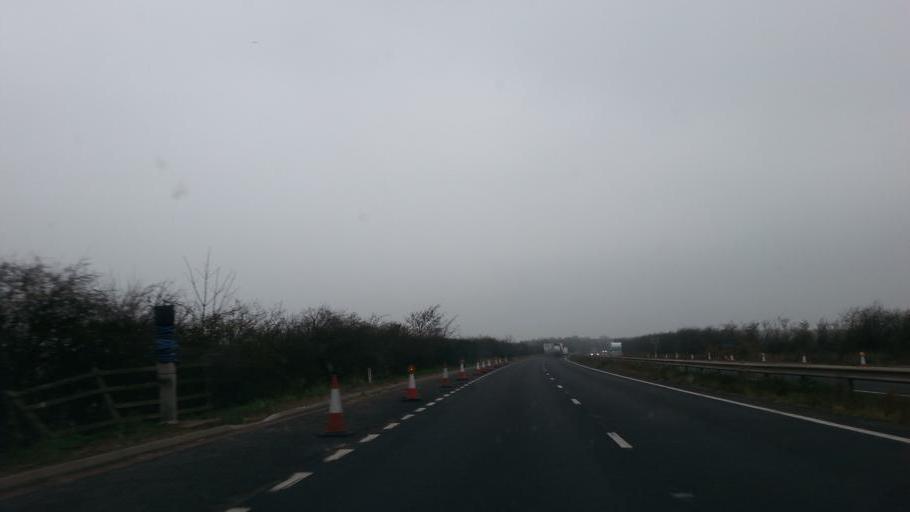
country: GB
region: England
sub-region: Cambridgeshire
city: Fulbourn
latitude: 52.2152
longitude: 0.2006
